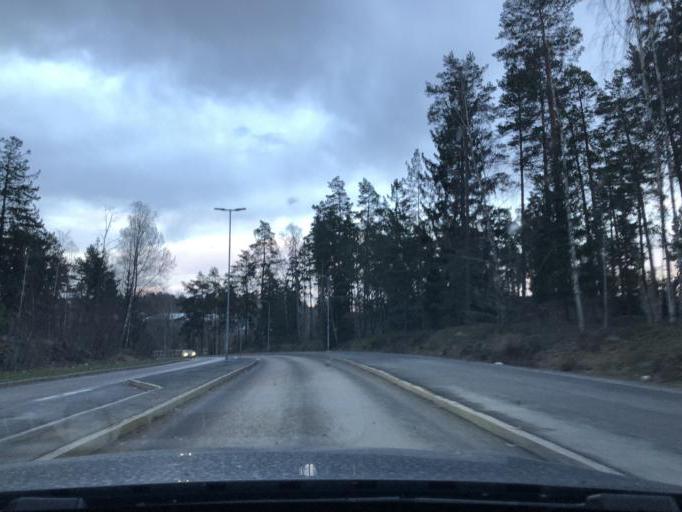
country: SE
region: Stockholm
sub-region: Sodertalje Kommun
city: Soedertaelje
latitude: 59.1773
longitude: 17.6101
